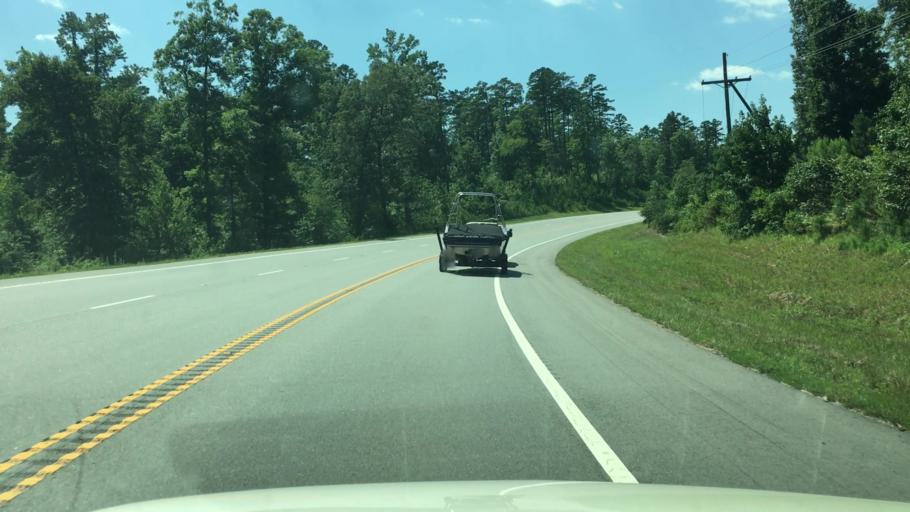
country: US
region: Arkansas
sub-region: Garland County
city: Rockwell
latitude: 34.5184
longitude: -93.3128
